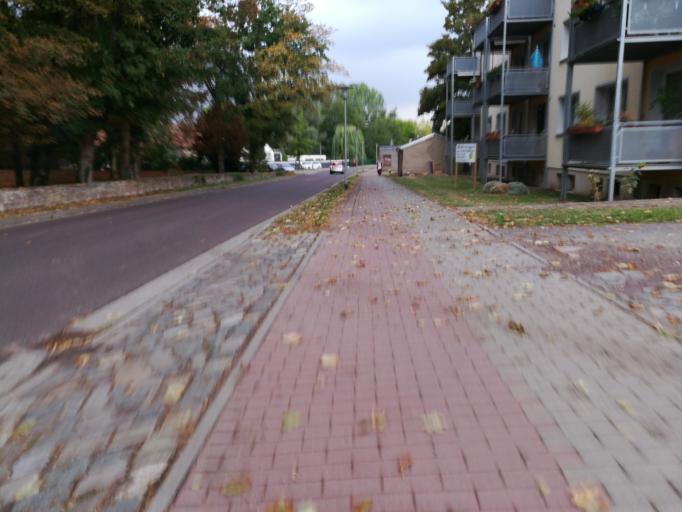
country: DE
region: Saxony-Anhalt
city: Eichenbarleben
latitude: 52.1651
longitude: 11.4010
